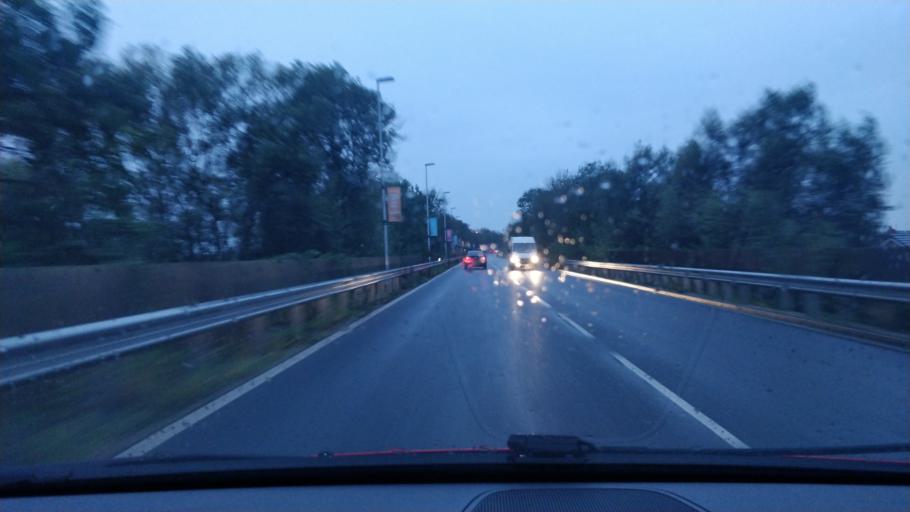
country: GB
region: England
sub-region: Lancashire
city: Great Marton
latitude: 53.7929
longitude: -3.0340
